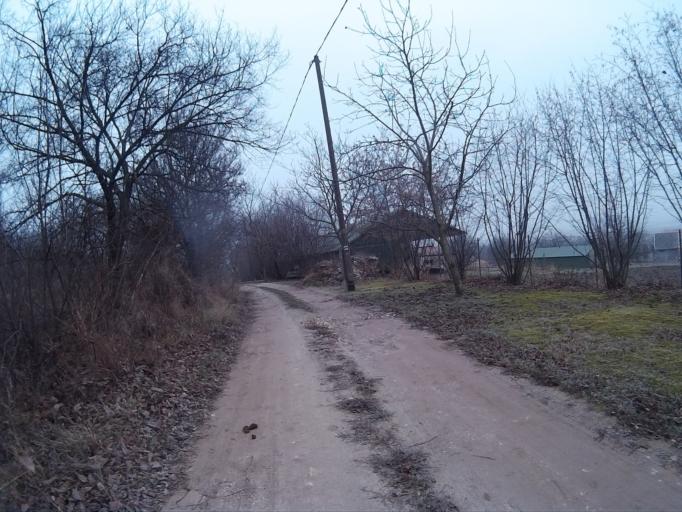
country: HU
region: Fejer
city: Csakvar
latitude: 47.3808
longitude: 18.4400
